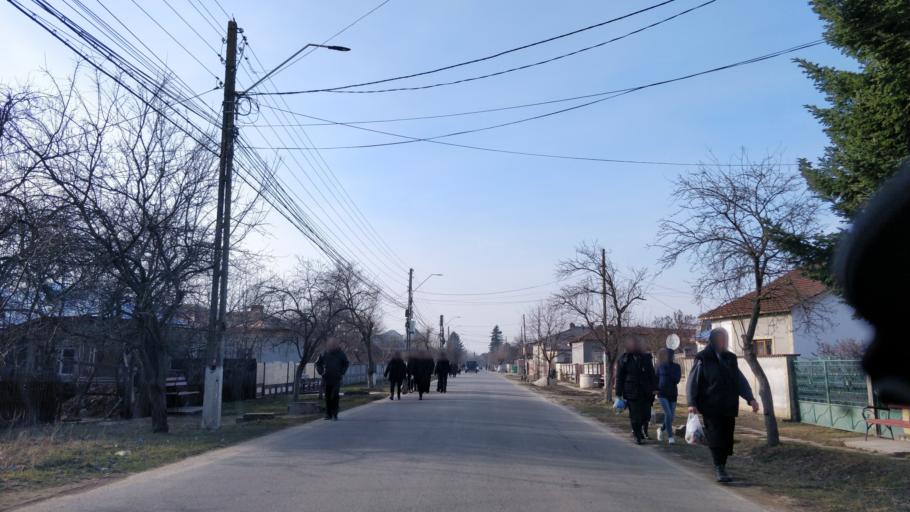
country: RO
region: Giurgiu
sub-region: Comuna Ulmi
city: Trestieni
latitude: 44.5013
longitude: 25.7624
